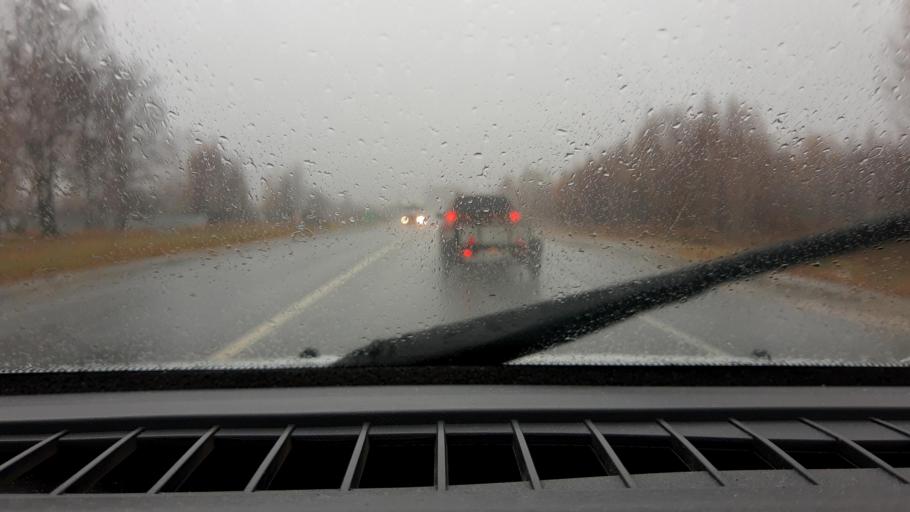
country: RU
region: Nizjnij Novgorod
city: Sitniki
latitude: 56.5286
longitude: 44.0250
